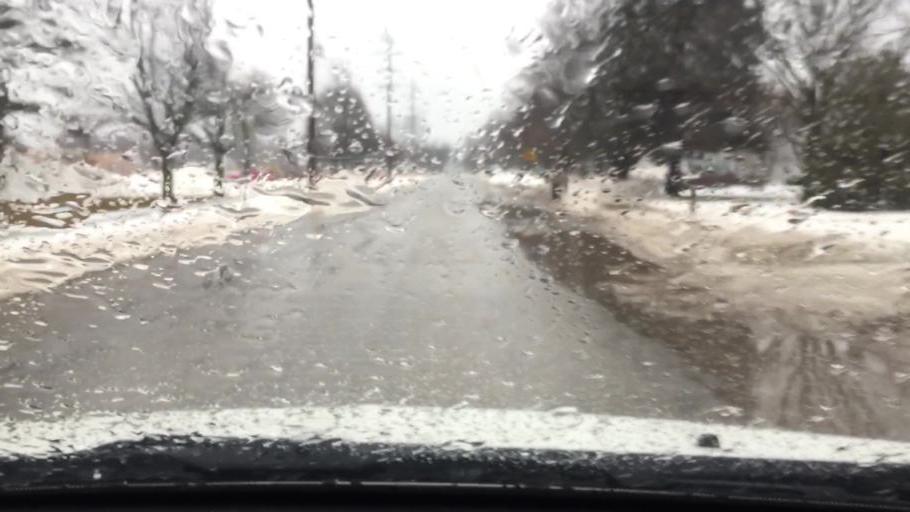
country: US
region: Michigan
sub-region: Charlevoix County
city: Charlevoix
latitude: 45.3091
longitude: -85.2554
